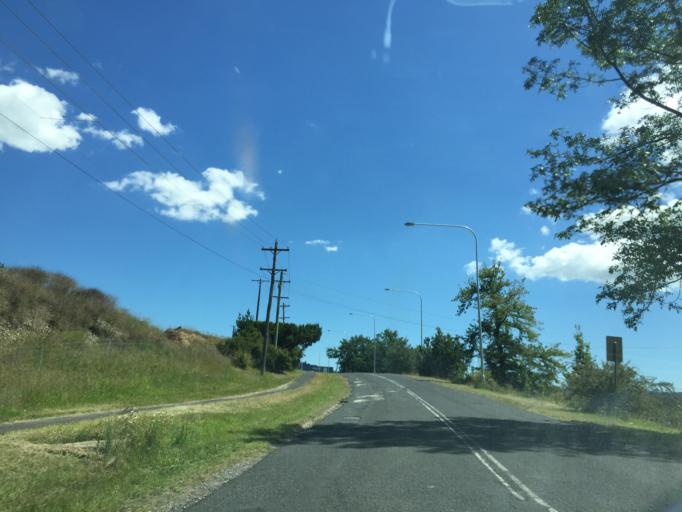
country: AU
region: New South Wales
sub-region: Lithgow
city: Portland
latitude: -33.4051
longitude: 150.0700
